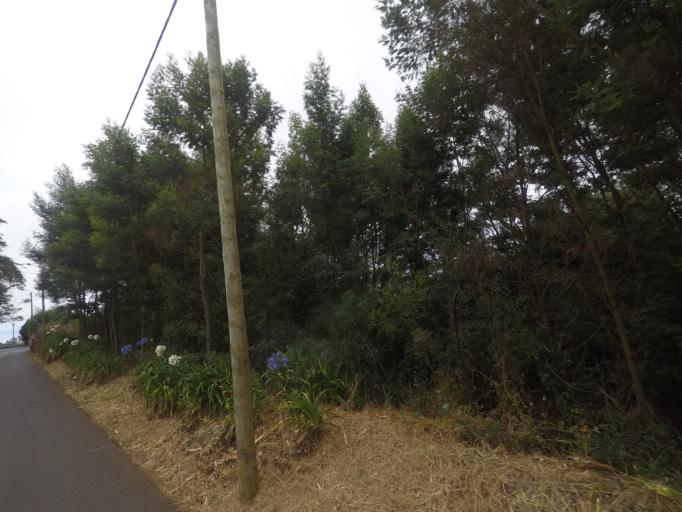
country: PT
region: Madeira
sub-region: Funchal
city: Nossa Senhora do Monte
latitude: 32.6674
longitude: -16.8786
